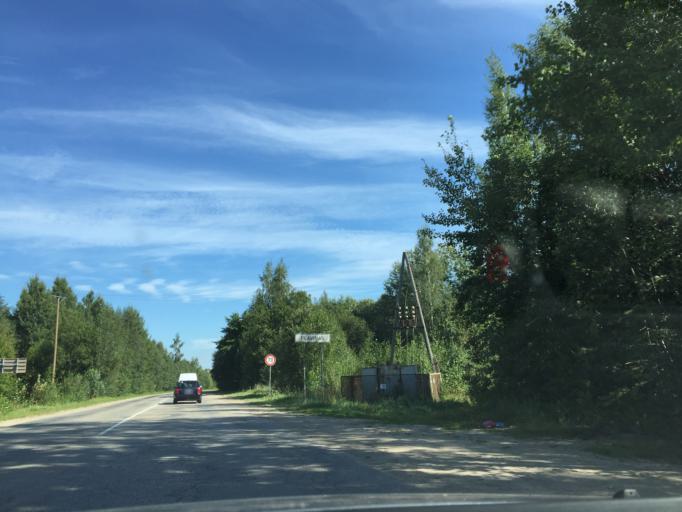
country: LV
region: Plavinu
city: Plavinas
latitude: 56.6055
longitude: 25.6788
